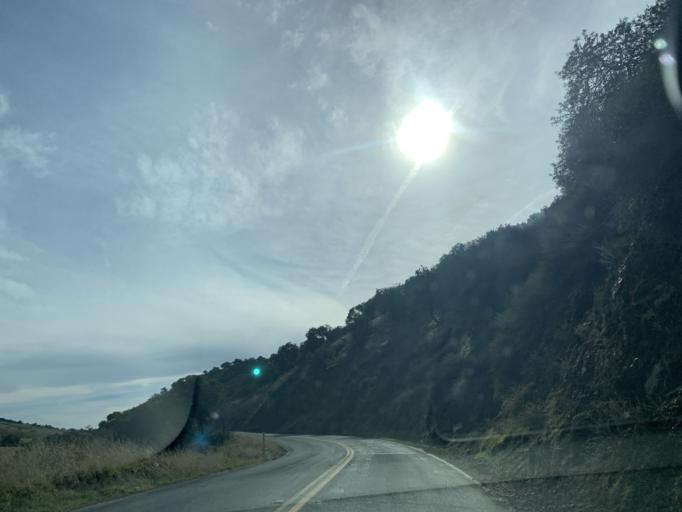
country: US
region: California
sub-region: Monterey County
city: Greenfield
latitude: 36.4438
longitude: -121.0419
